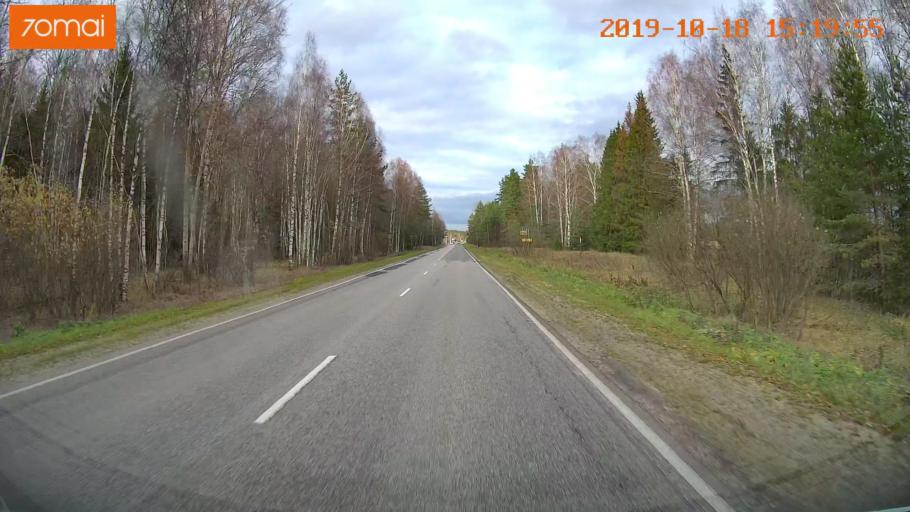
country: RU
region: Vladimir
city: Anopino
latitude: 55.6801
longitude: 40.7412
